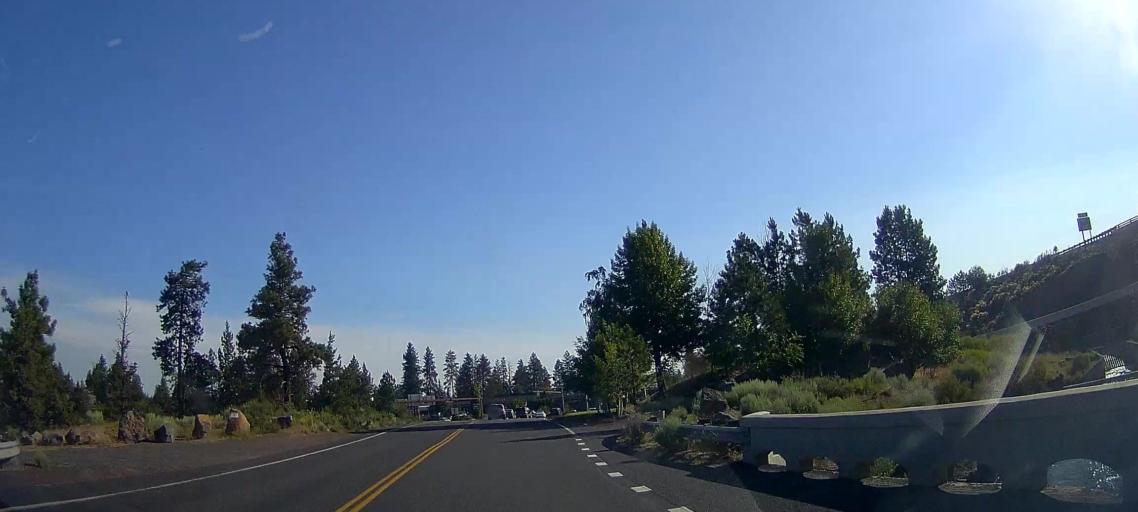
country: US
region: Oregon
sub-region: Deschutes County
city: Bend
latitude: 44.0768
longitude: -121.3052
